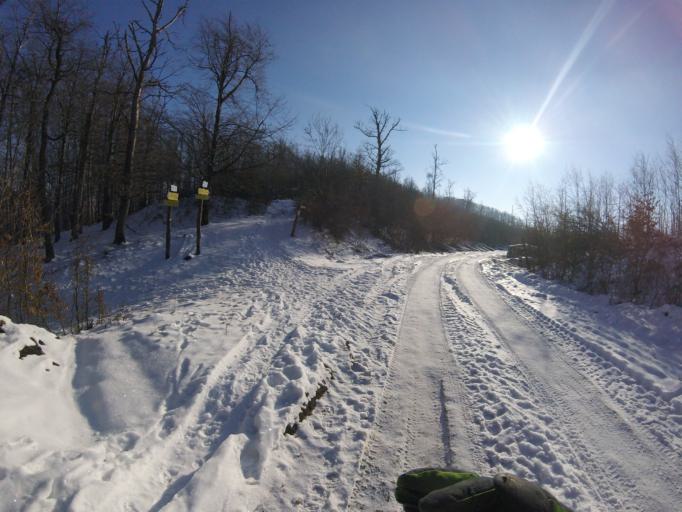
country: HU
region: Heves
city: Parad
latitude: 47.8706
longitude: 20.0433
